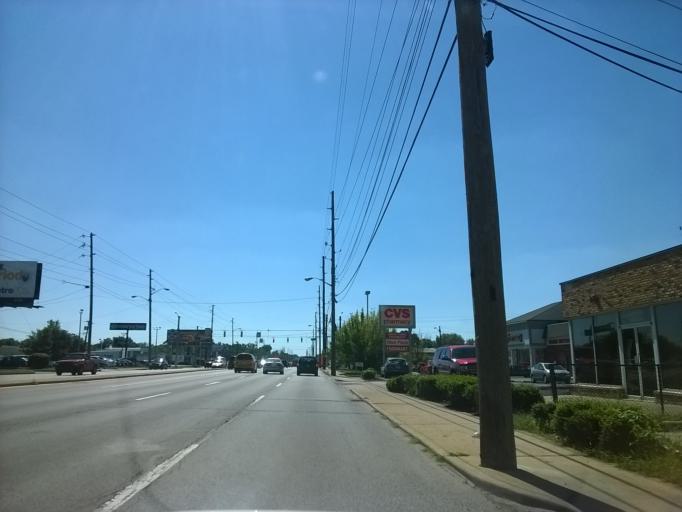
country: US
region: Indiana
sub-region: Marion County
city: Broad Ripple
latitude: 39.8414
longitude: -86.1221
